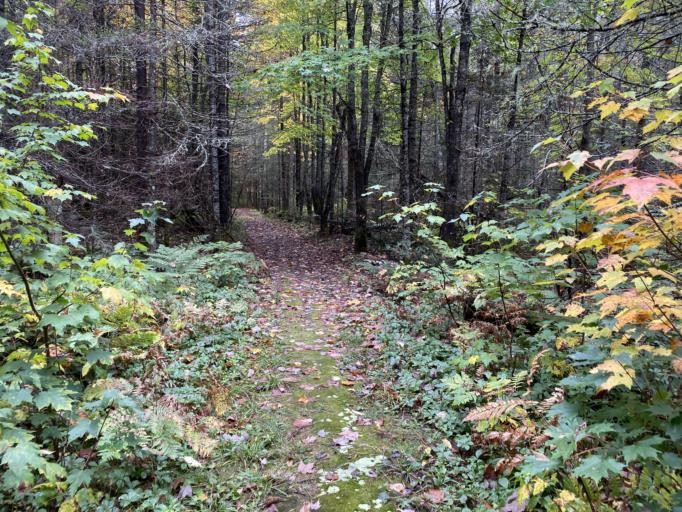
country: US
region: Michigan
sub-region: Marquette County
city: West Ishpeming
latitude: 46.5357
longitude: -87.9999
